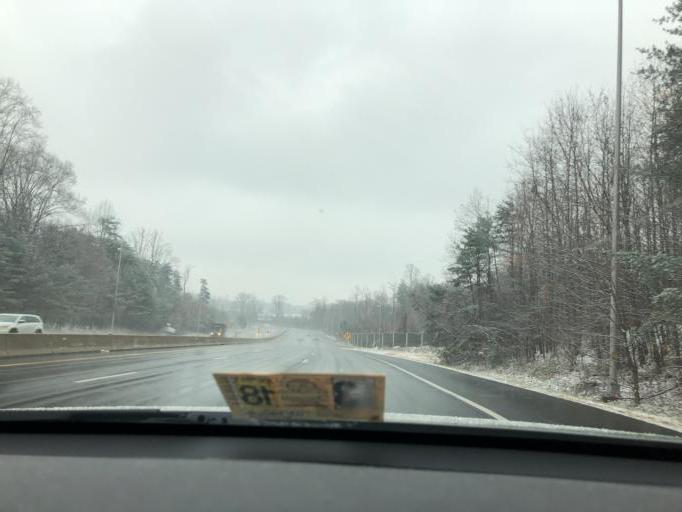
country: US
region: Virginia
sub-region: Fairfax County
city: Greenbriar
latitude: 38.8528
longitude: -77.3880
